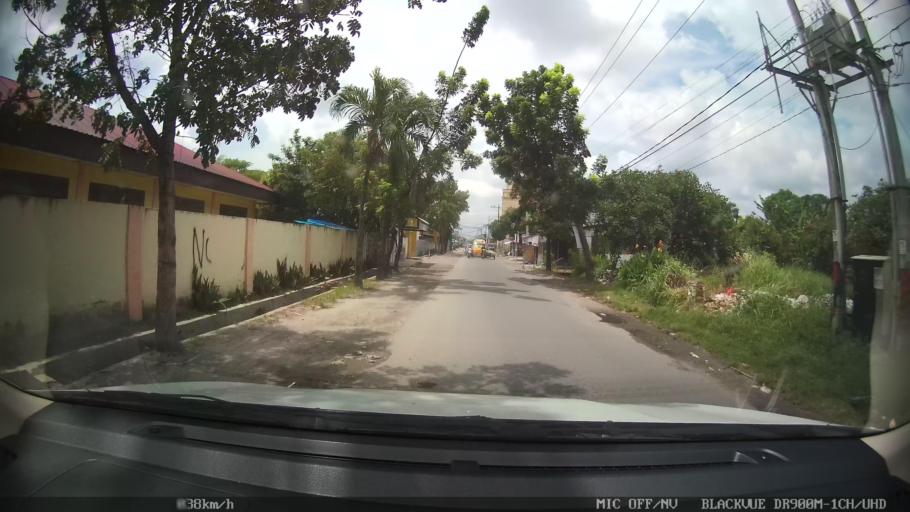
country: ID
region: North Sumatra
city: Medan
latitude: 3.6220
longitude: 98.7484
